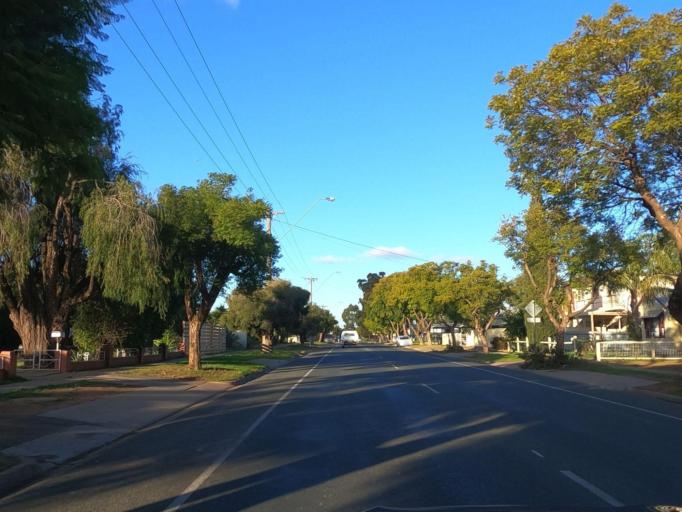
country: AU
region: Victoria
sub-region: Swan Hill
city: Swan Hill
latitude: -35.3474
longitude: 143.5533
